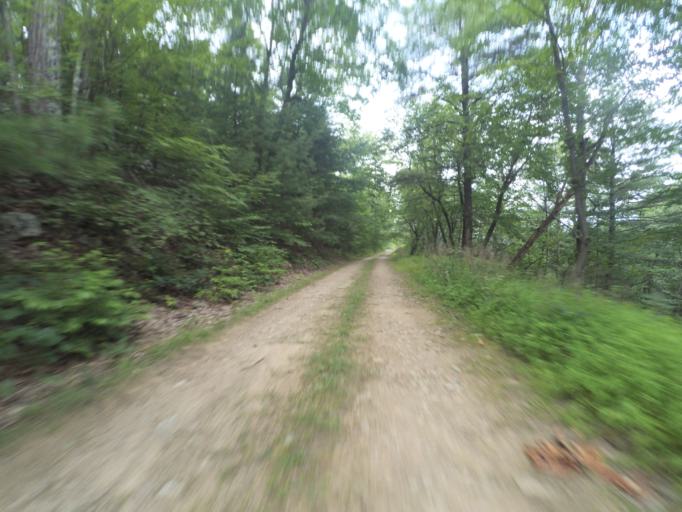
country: US
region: Pennsylvania
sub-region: Centre County
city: Boalsburg
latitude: 40.7118
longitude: -77.7690
